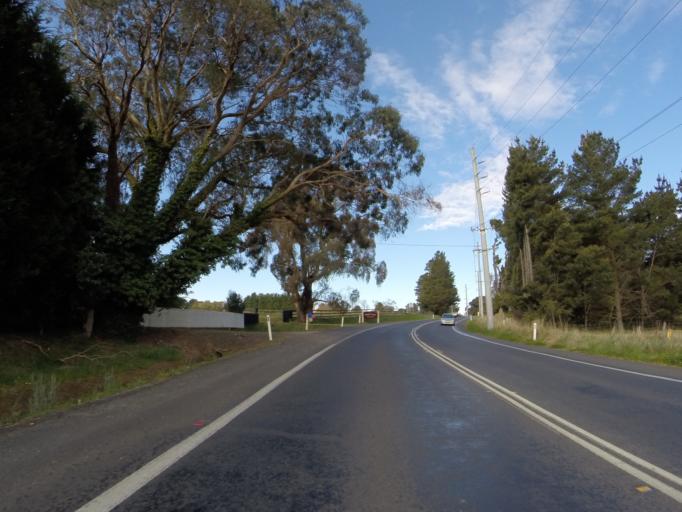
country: AU
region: New South Wales
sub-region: Wingecarribee
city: Moss Vale
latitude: -34.5551
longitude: 150.3527
